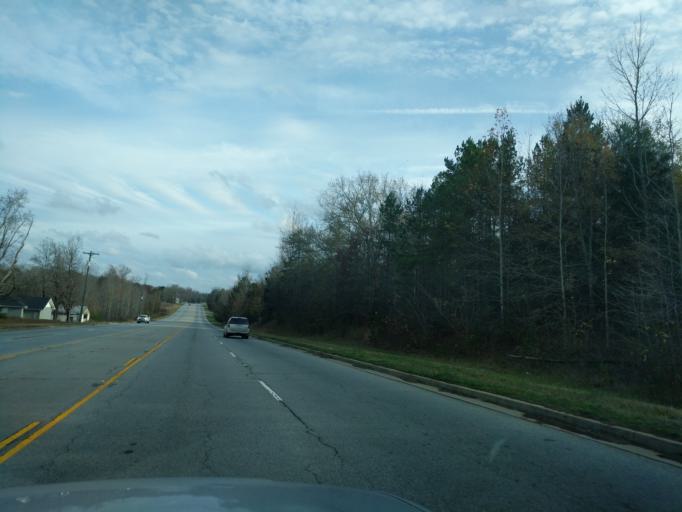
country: US
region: South Carolina
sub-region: Anderson County
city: Honea Path
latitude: 34.5111
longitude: -82.3059
